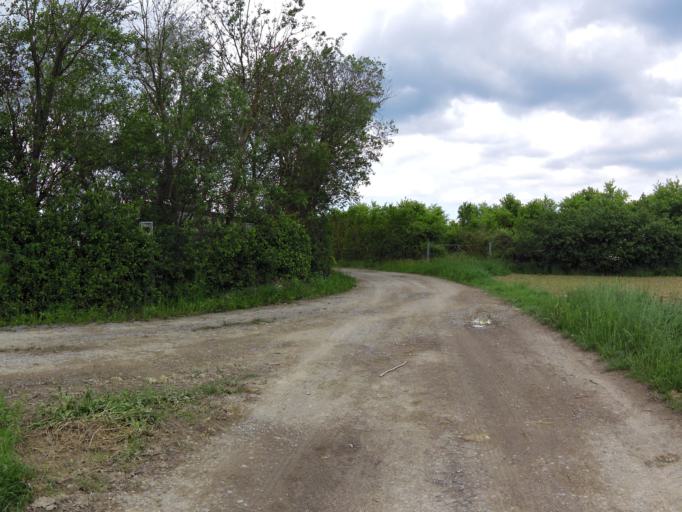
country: DE
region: Bavaria
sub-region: Regierungsbezirk Unterfranken
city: Winterhausen
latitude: 49.7250
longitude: 10.0272
